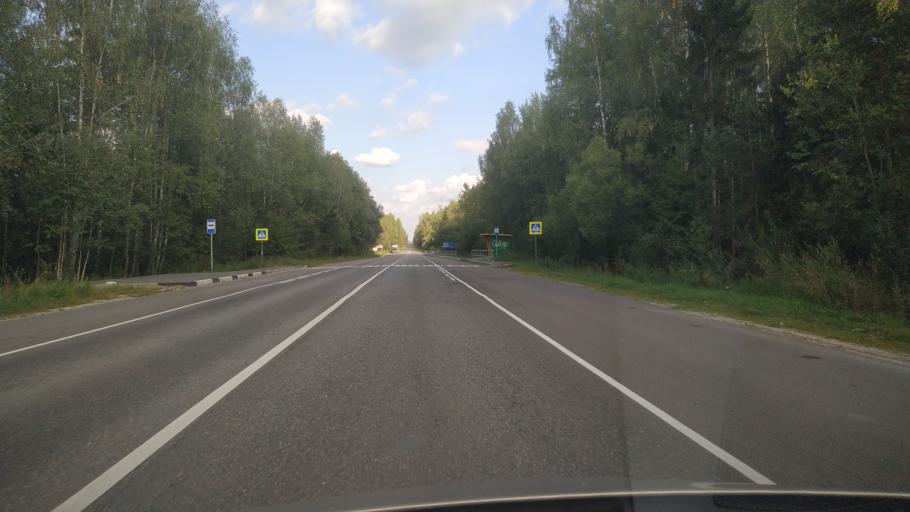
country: RU
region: Moskovskaya
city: Vereya
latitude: 55.7029
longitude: 39.1834
